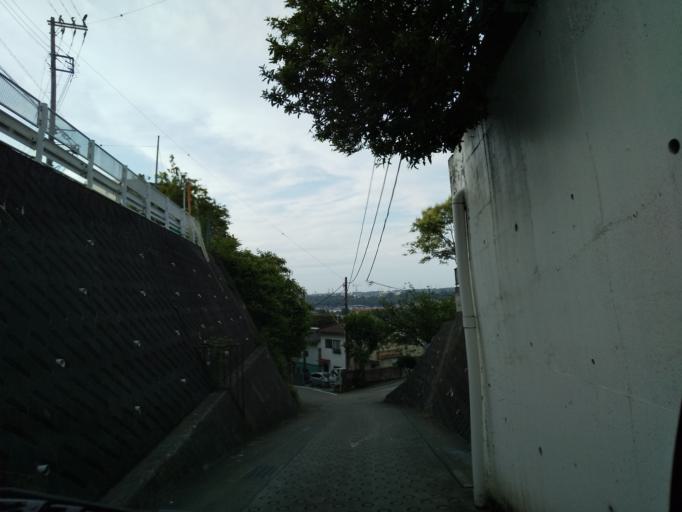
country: JP
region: Kanagawa
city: Zama
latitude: 35.5119
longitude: 139.3622
